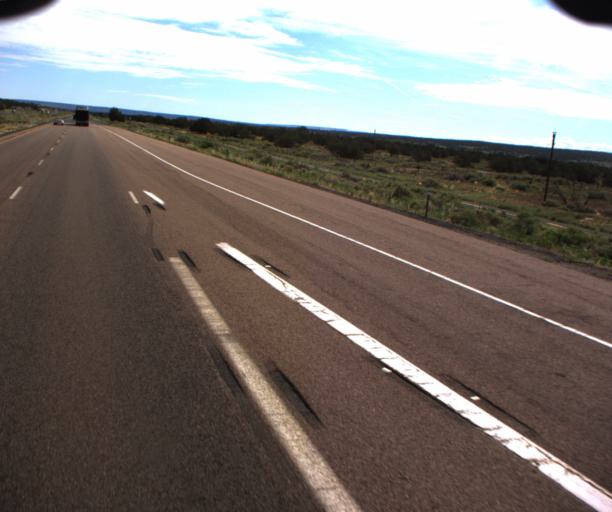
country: US
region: Arizona
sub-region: Apache County
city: Houck
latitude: 35.2412
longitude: -109.2985
